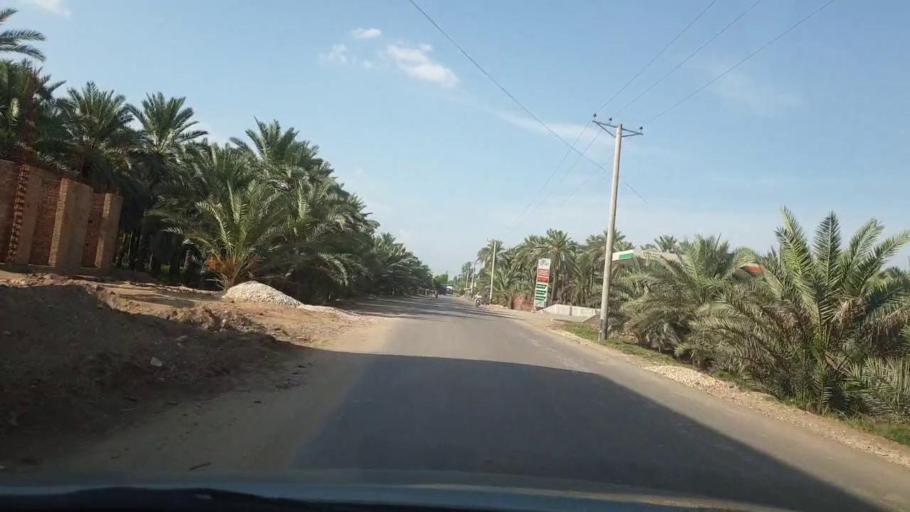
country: PK
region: Sindh
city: Sukkur
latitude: 27.6591
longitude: 68.8421
